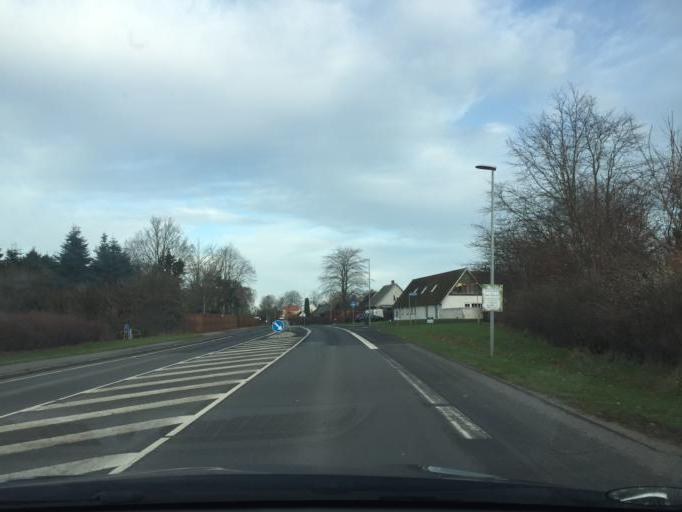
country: DK
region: South Denmark
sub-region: Faaborg-Midtfyn Kommune
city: Ringe
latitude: 55.2286
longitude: 10.4663
